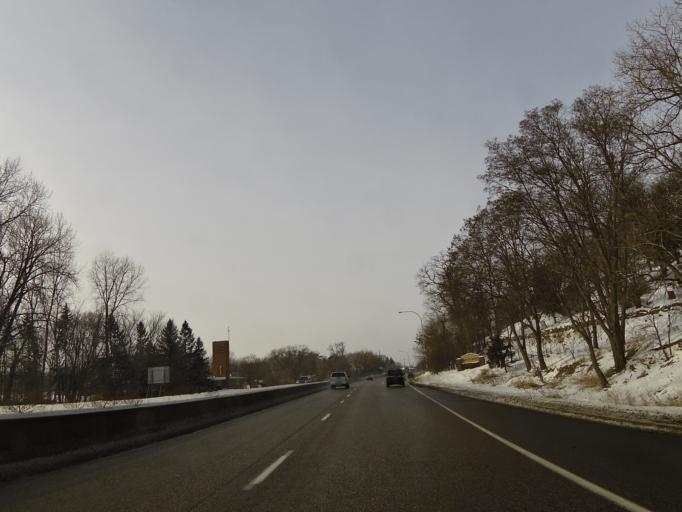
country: US
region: Minnesota
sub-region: Hennepin County
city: Excelsior
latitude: 44.9017
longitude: -93.5531
